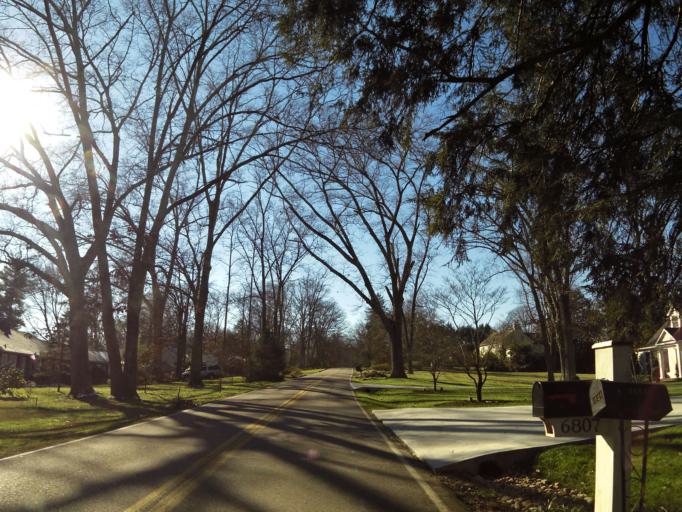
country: US
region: Tennessee
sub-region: Knox County
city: Knoxville
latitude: 35.9213
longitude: -84.0097
